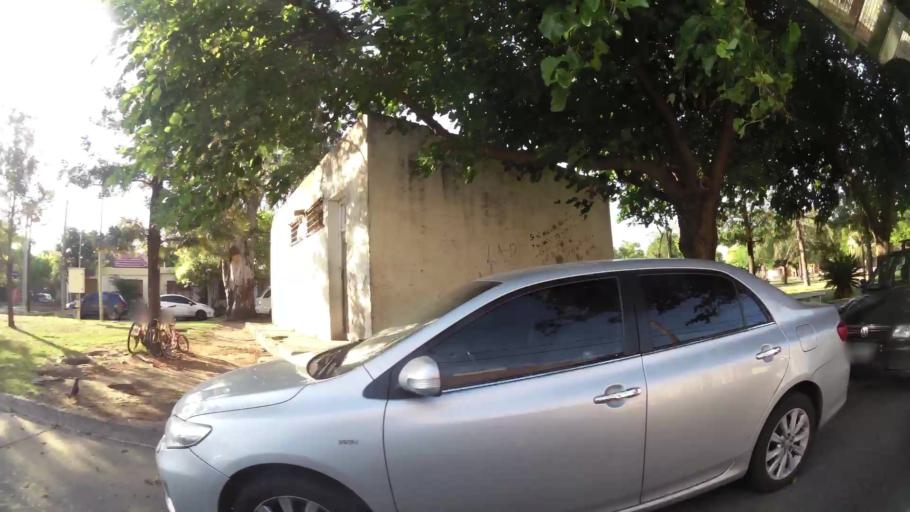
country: AR
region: Cordoba
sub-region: Departamento de Capital
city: Cordoba
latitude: -31.3920
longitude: -64.2191
